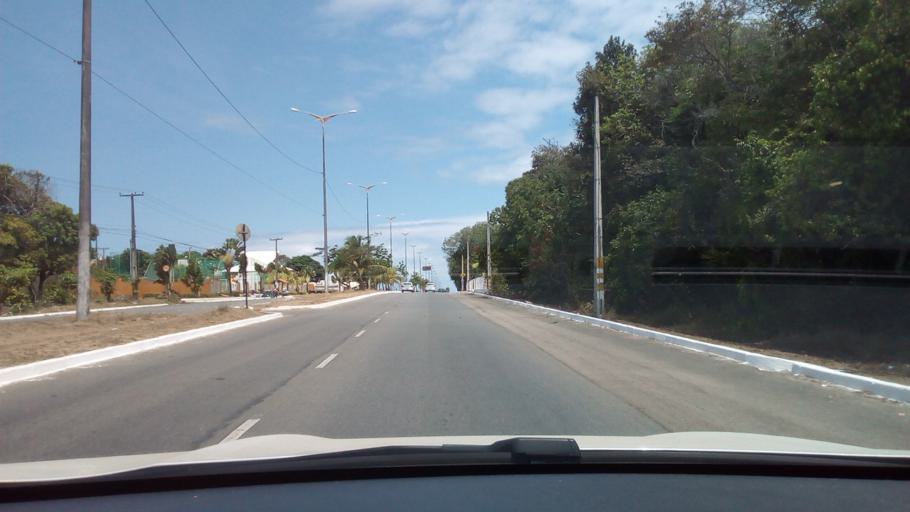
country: BR
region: Paraiba
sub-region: Joao Pessoa
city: Joao Pessoa
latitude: -7.1607
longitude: -34.8096
